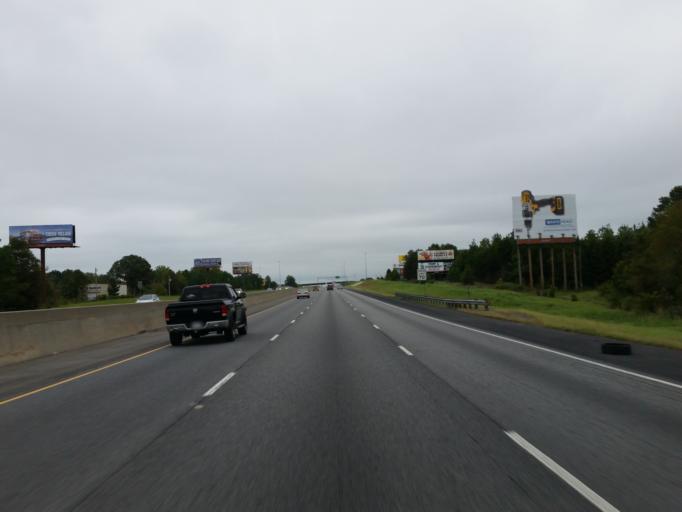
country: US
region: Georgia
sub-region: Crisp County
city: Cordele
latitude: 31.8443
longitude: -83.7163
